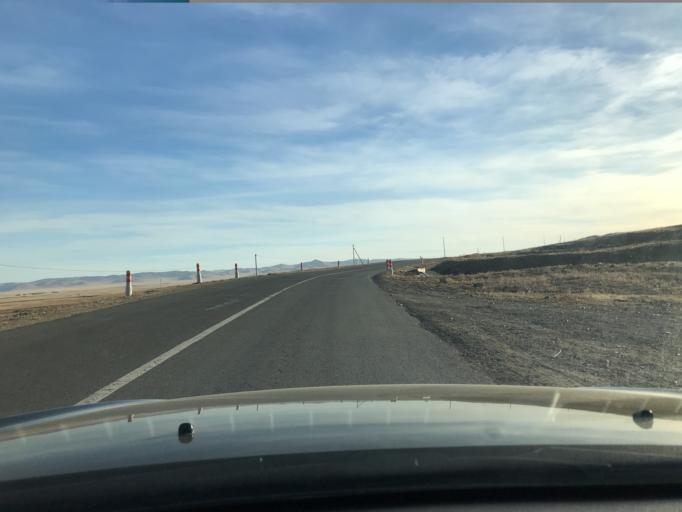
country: MN
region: Central Aimak
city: Dzuunmod
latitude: 47.7912
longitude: 107.3222
